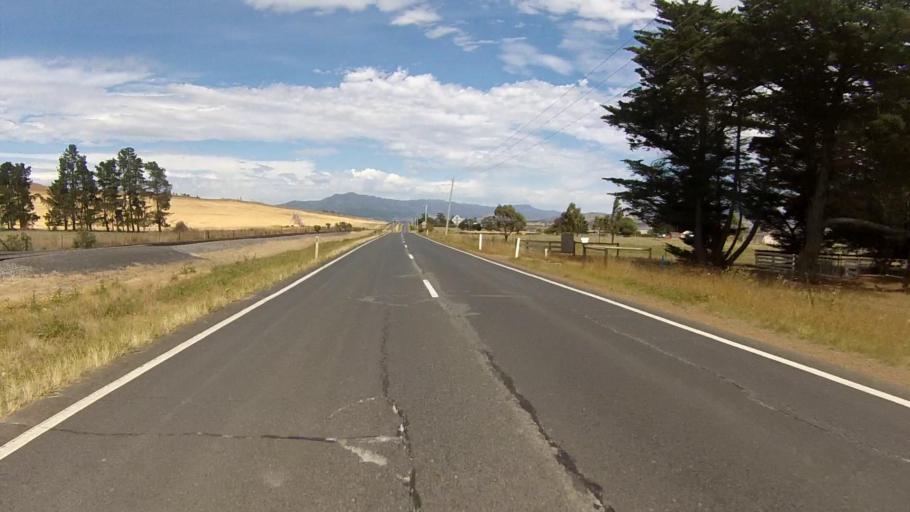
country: AU
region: Tasmania
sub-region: Brighton
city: Bridgewater
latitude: -42.6900
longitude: 147.3152
